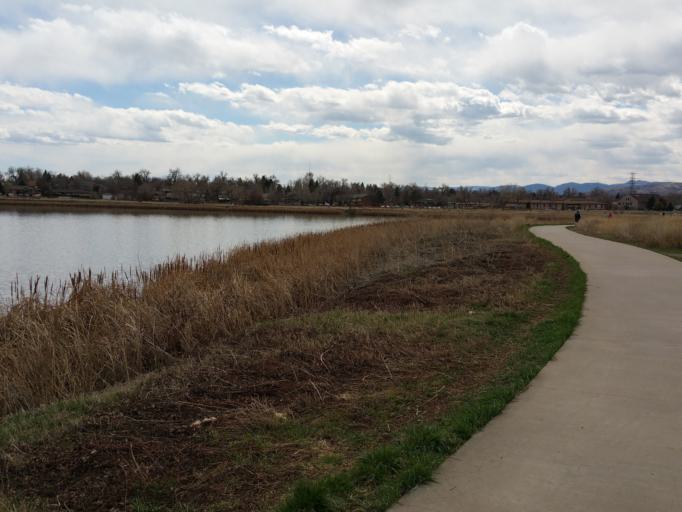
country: US
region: Colorado
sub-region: Jefferson County
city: Wheat Ridge
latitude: 39.7587
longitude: -105.1057
